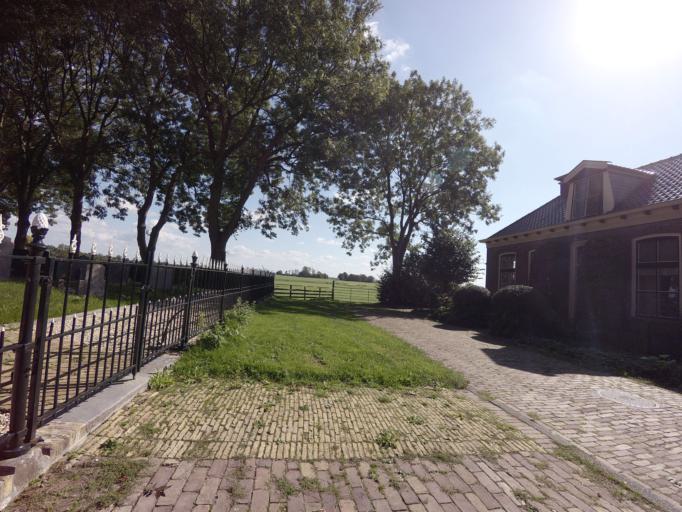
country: NL
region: Friesland
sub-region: Gemeente Littenseradiel
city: Makkum
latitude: 53.1121
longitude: 5.6765
